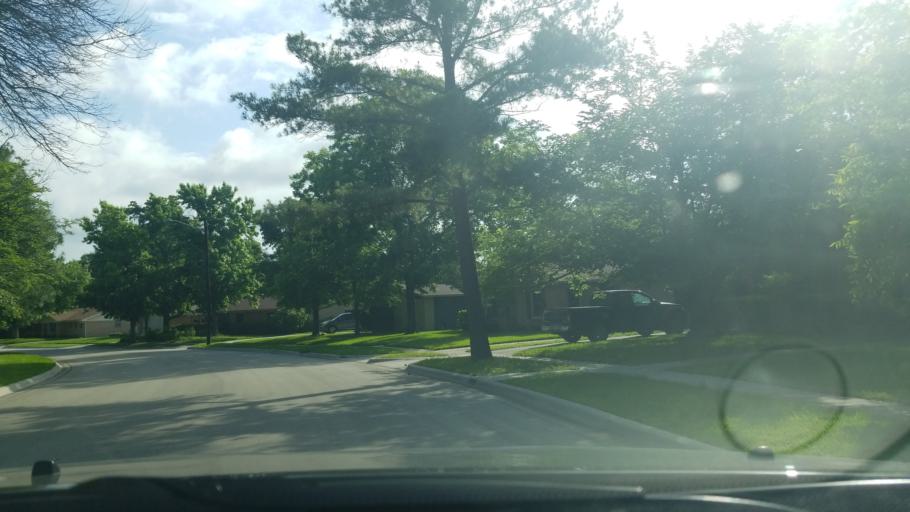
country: US
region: Texas
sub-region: Denton County
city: Denton
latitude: 33.2260
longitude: -97.1581
